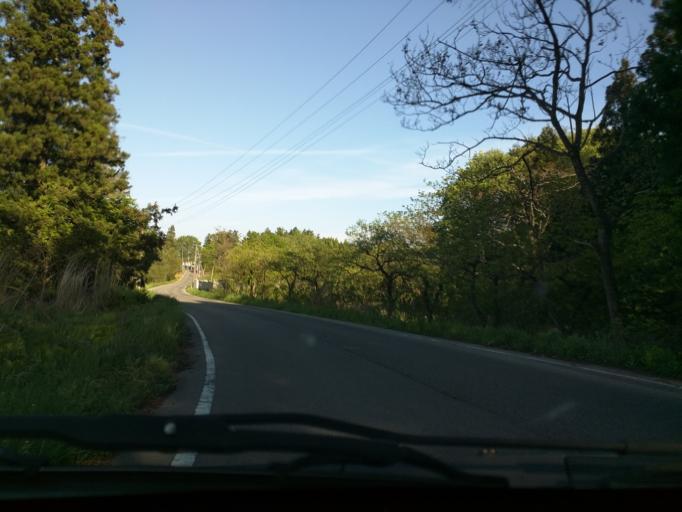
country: JP
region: Fukushima
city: Kitakata
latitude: 37.5220
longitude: 139.8026
